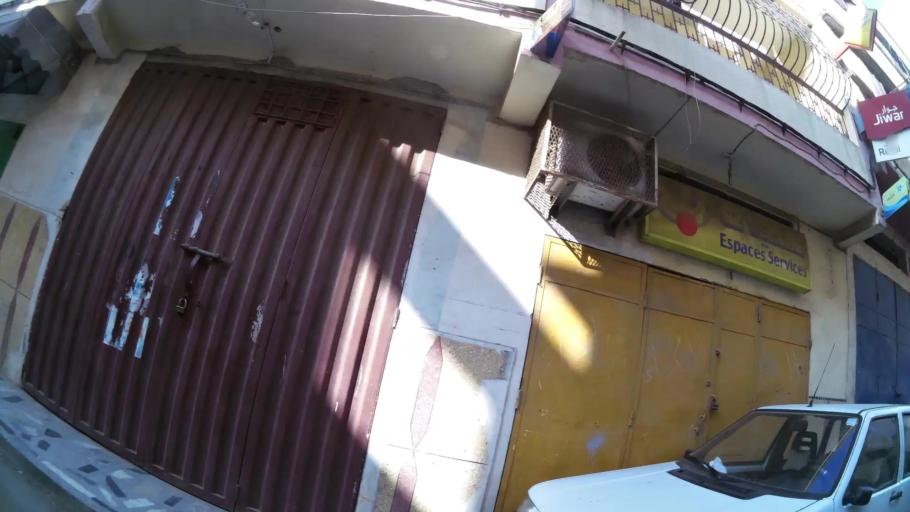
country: MA
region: Rabat-Sale-Zemmour-Zaer
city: Sale
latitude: 34.0532
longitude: -6.7754
